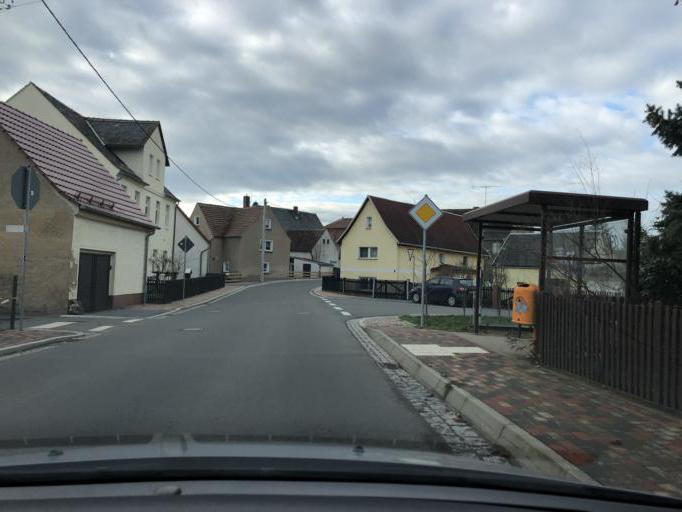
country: DE
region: Saxony
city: Grossbothen
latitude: 51.1825
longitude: 12.7858
